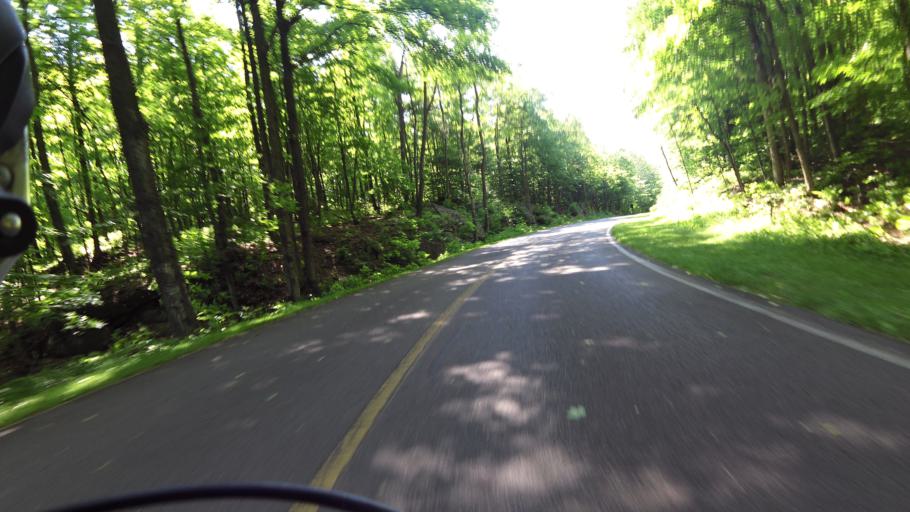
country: CA
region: Quebec
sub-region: Outaouais
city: Wakefield
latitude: 45.5212
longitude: -75.8551
